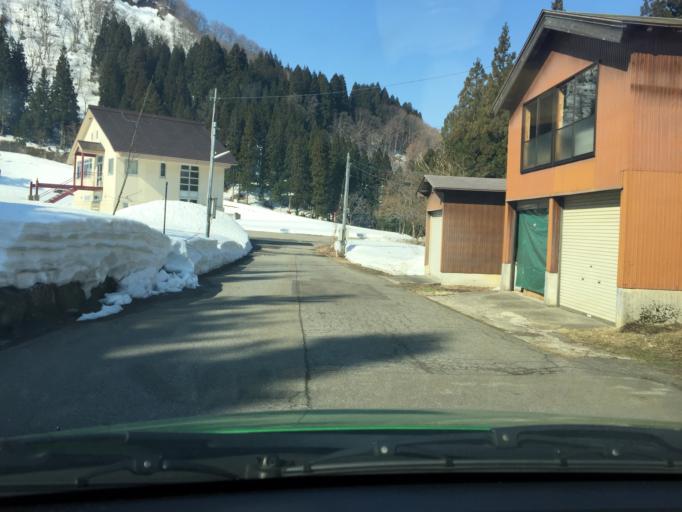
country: JP
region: Ishikawa
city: Tsurugi-asahimachi
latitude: 36.2720
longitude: 136.7038
